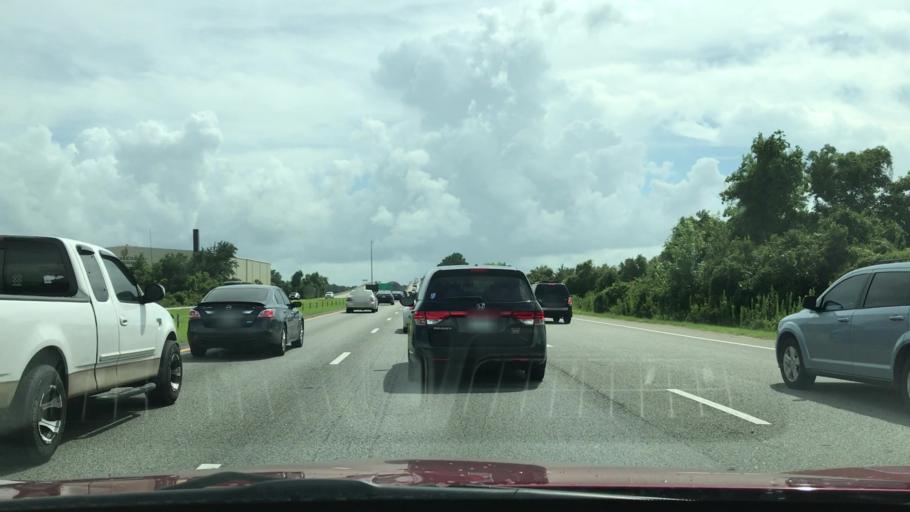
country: US
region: South Carolina
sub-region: Charleston County
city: North Charleston
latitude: 32.8400
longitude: -80.0207
